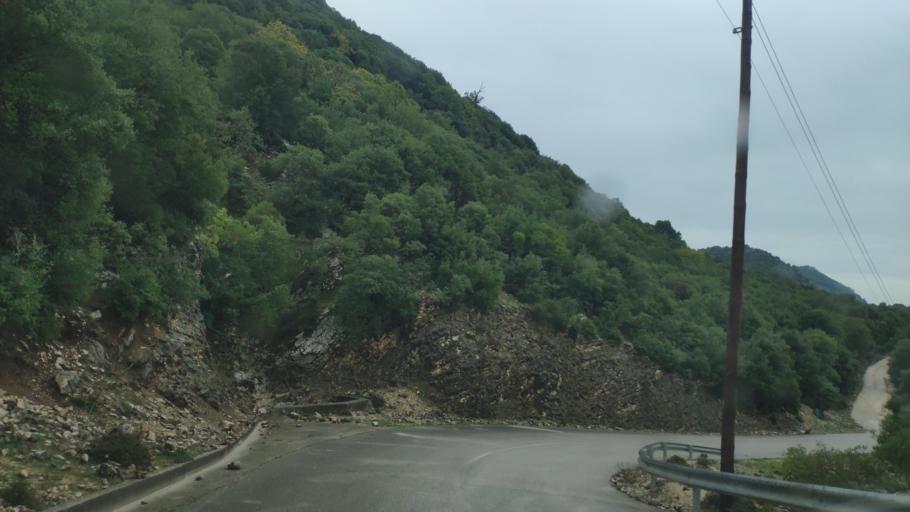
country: GR
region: Epirus
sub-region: Nomos Thesprotias
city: Paramythia
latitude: 39.3949
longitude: 20.6238
